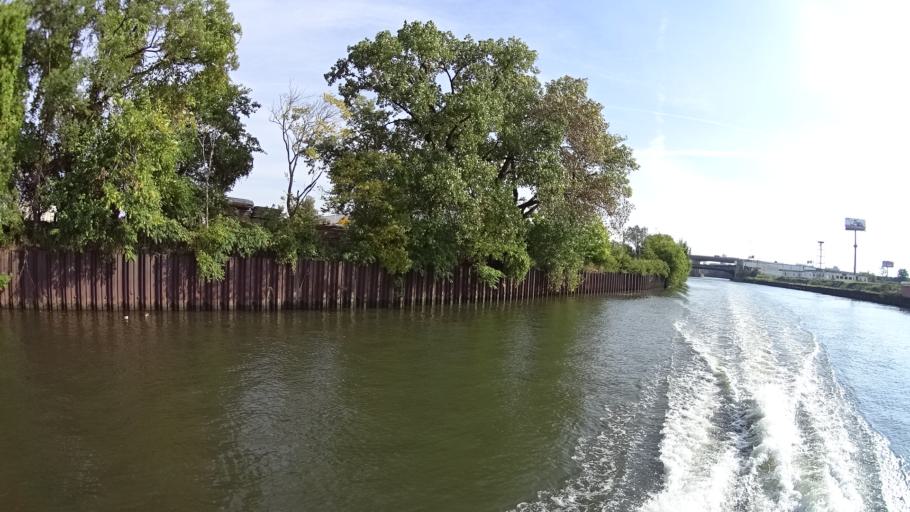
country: US
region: Illinois
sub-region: Cook County
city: Chicago
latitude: 41.8482
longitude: -87.6503
